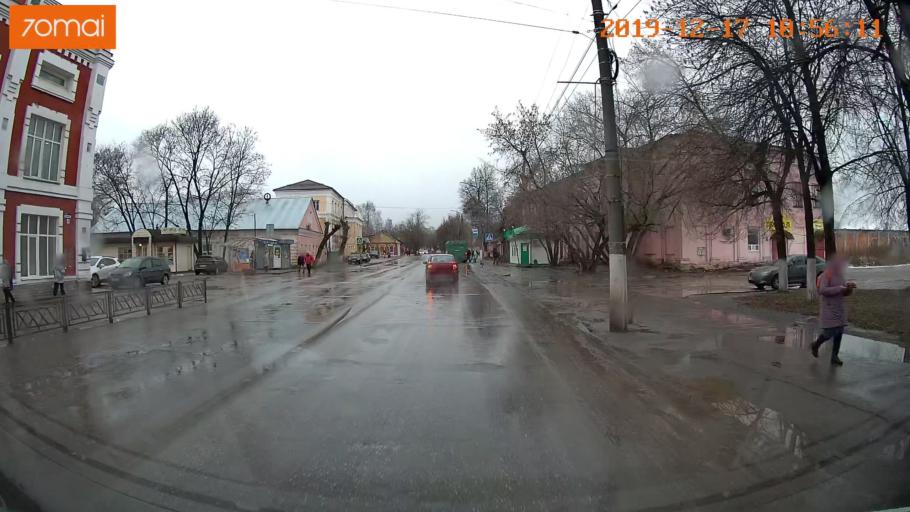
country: RU
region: Vladimir
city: Gus'-Khrustal'nyy
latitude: 55.6173
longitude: 40.6650
